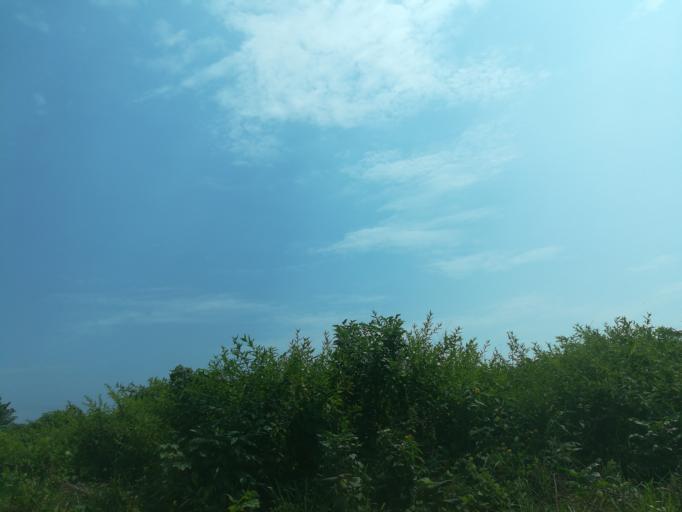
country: NG
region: Lagos
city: Ikorodu
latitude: 6.5934
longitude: 3.6391
